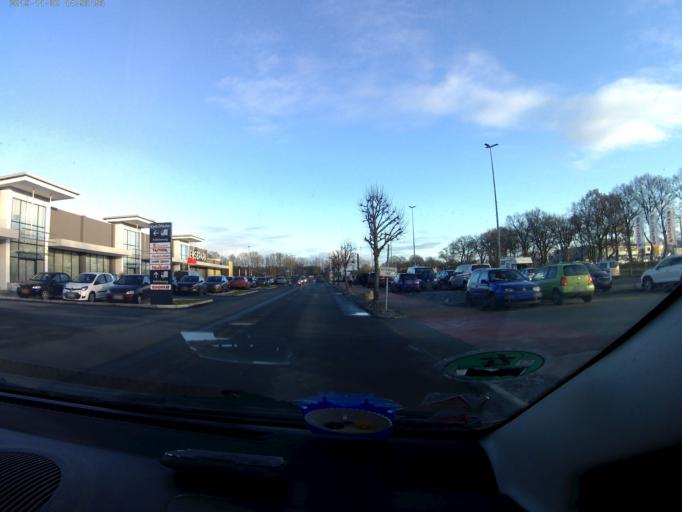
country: DE
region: Lower Saxony
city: Leer
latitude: 53.2598
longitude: 7.4560
